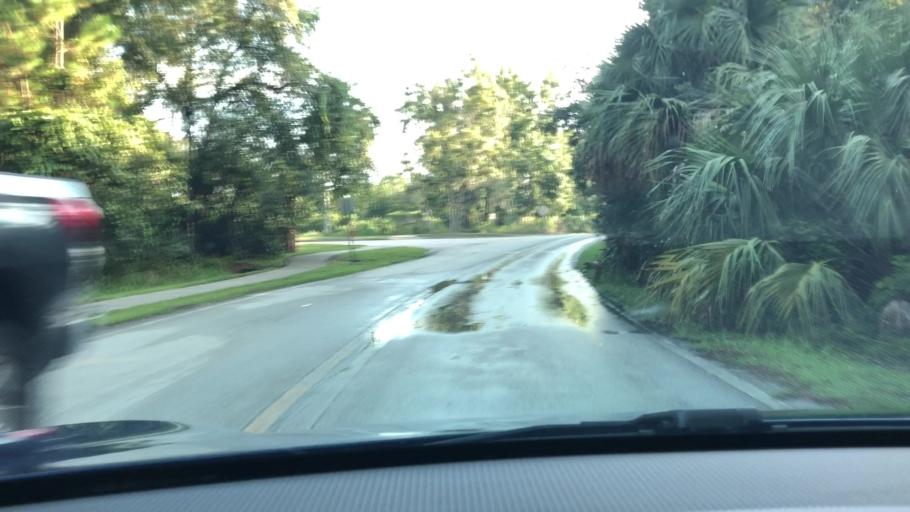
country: US
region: Florida
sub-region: Seminole County
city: Sanford
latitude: 28.7766
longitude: -81.2878
